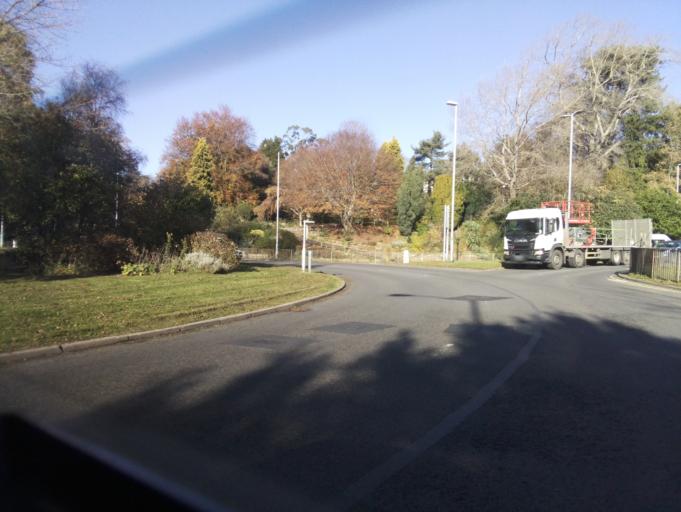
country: GB
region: England
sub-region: Somerset
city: Yeovil
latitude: 50.9463
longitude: -2.6369
